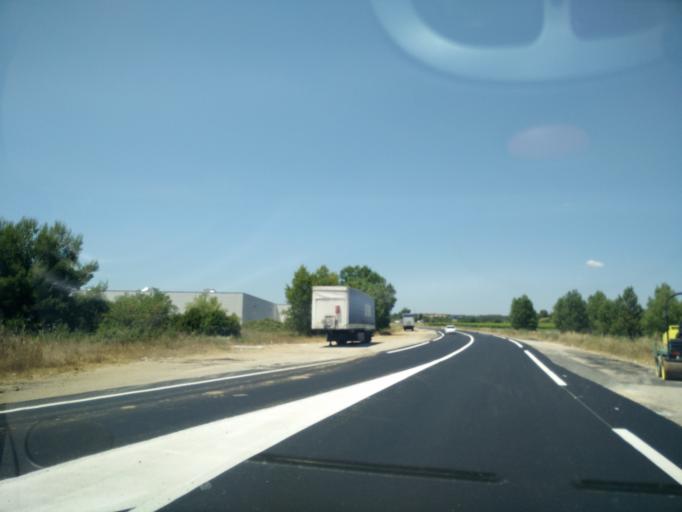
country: FR
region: Languedoc-Roussillon
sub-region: Departement de l'Herault
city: Lunel
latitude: 43.6918
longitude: 4.1443
